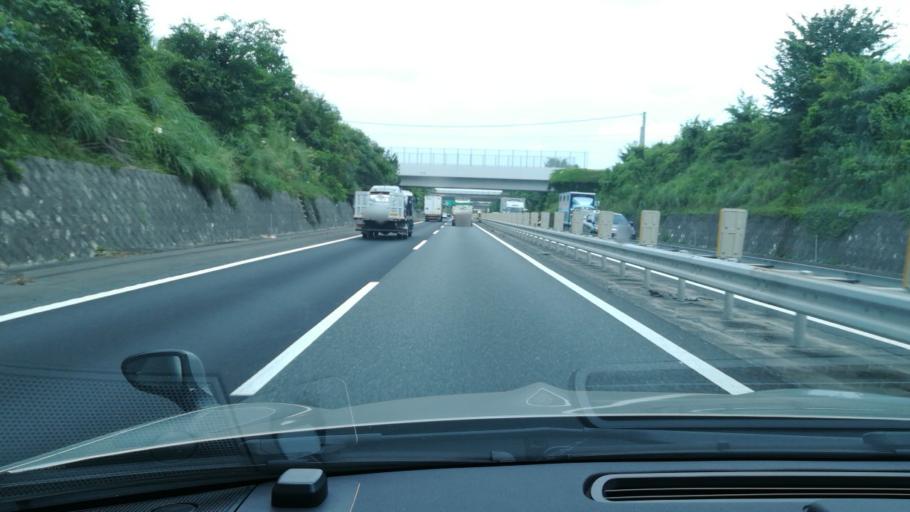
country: JP
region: Saitama
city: Hanno
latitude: 35.8020
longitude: 139.3318
